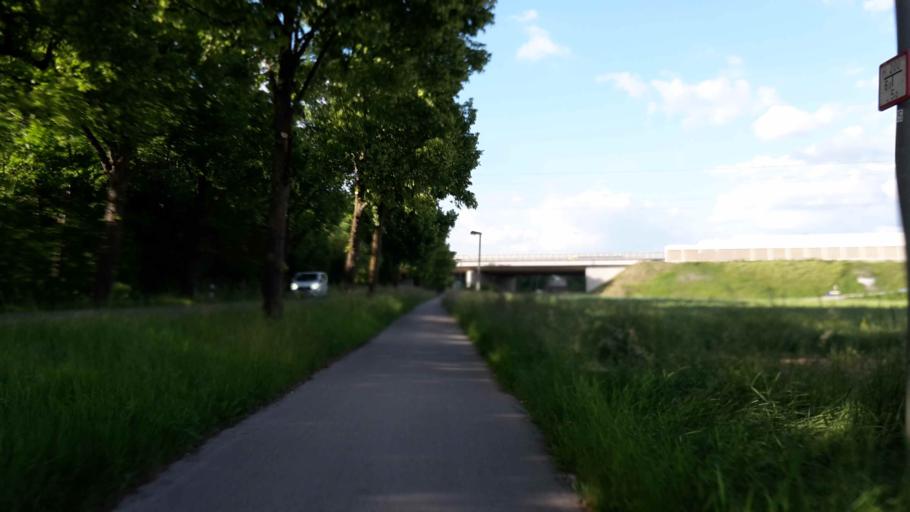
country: DE
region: Bavaria
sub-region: Upper Bavaria
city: Unterfoehring
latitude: 48.2040
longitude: 11.6522
